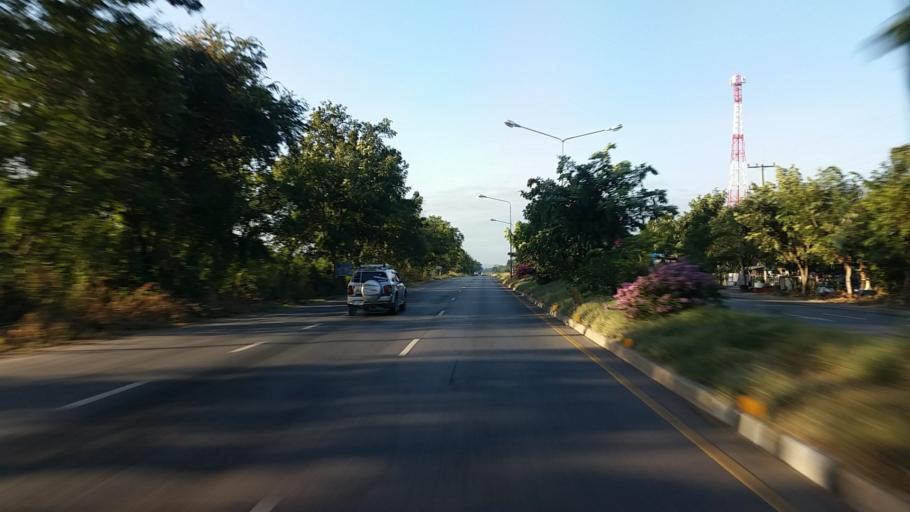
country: TH
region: Lop Buri
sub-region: Amphoe Tha Luang
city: Tha Luang
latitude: 15.1247
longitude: 101.0356
